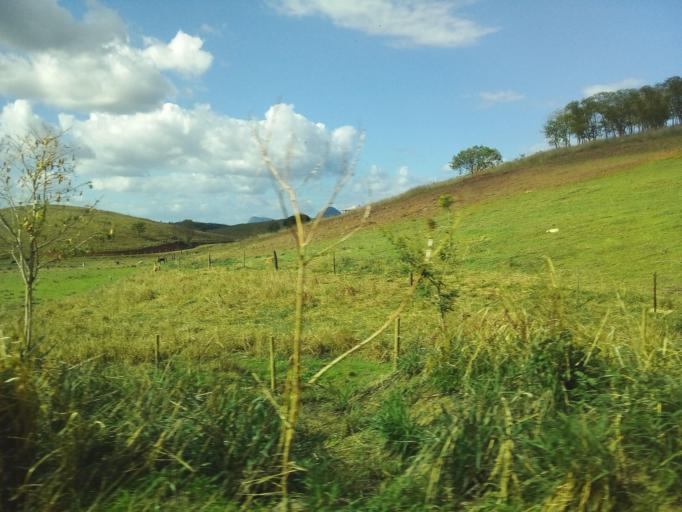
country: BR
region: Minas Gerais
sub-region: Conselheiro Pena
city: Conselheiro Pena
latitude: -18.9823
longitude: -41.6157
